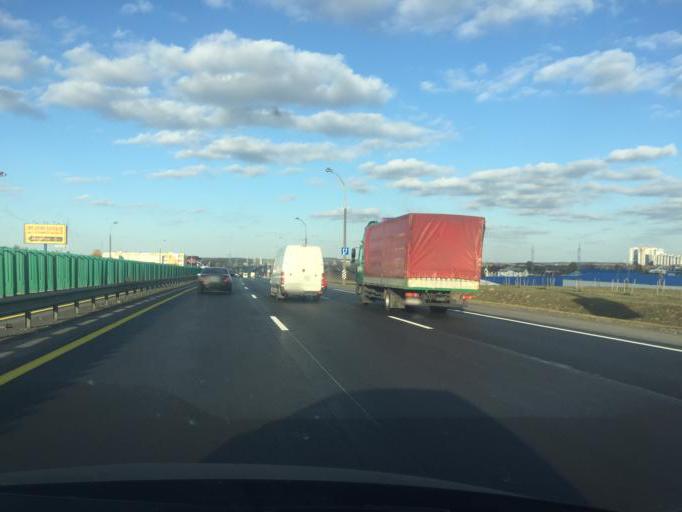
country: BY
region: Minsk
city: Zhdanovichy
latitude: 53.9348
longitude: 27.4255
